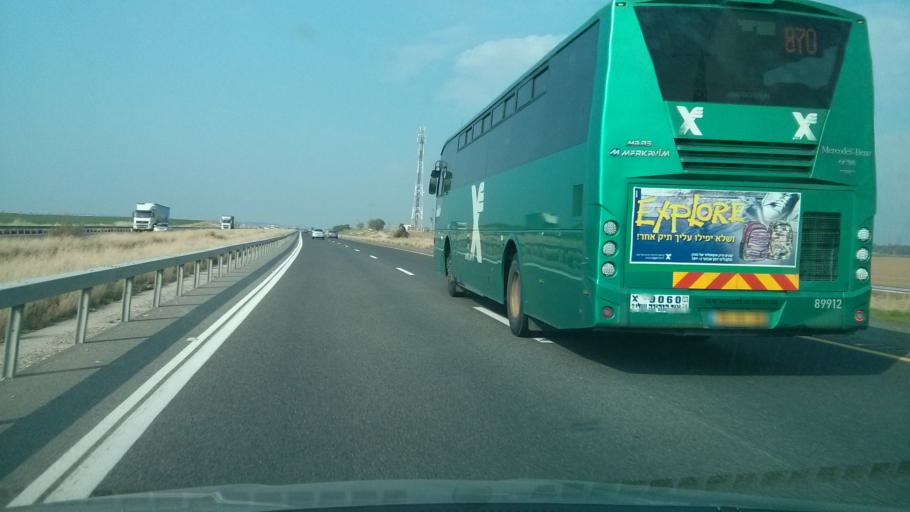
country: IL
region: Central District
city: Bene 'Ayish
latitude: 31.7128
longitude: 34.8205
